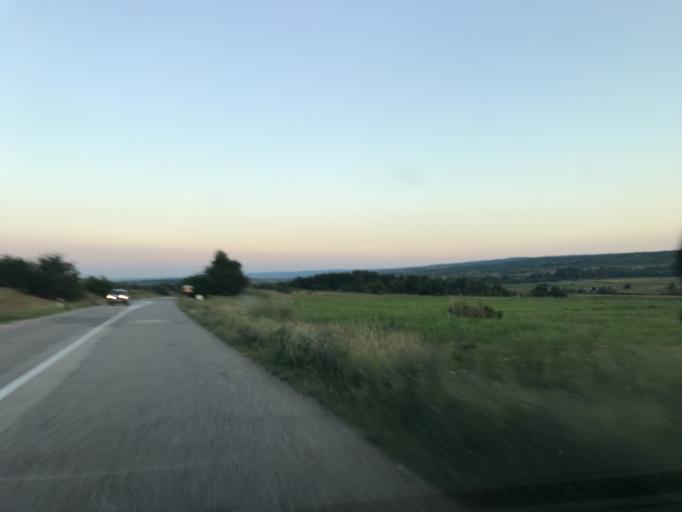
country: RO
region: Mehedinti
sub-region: Comuna Gogosu
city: Ostrovu Mare
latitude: 44.3075
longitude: 22.5055
